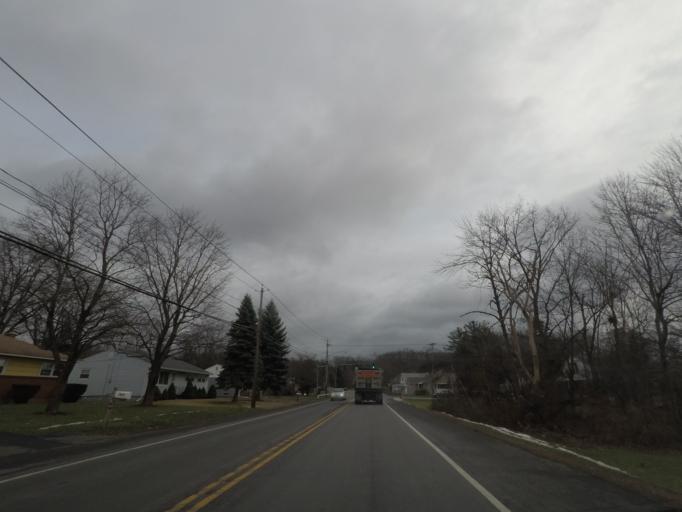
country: US
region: New York
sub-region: Rensselaer County
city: Hampton Manor
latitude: 42.6275
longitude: -73.7268
